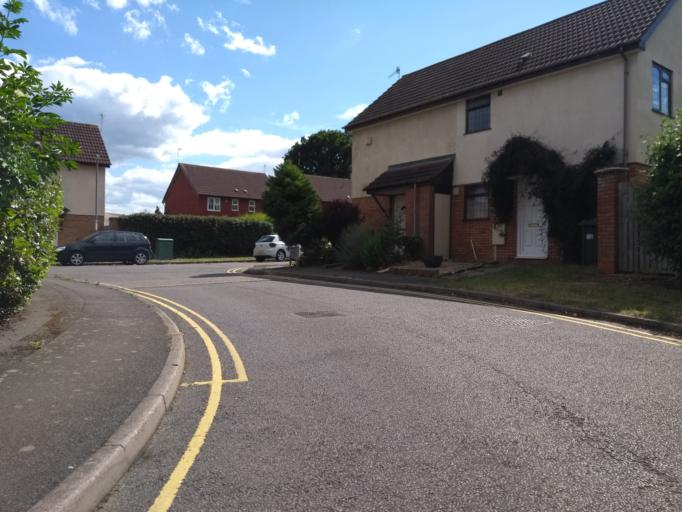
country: GB
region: England
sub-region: Warwickshire
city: Warwick
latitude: 52.2855
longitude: -1.5959
